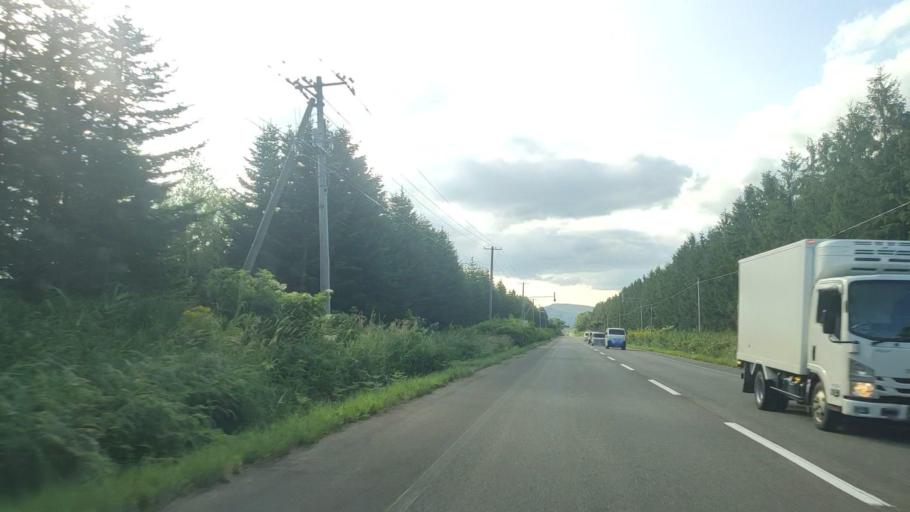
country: JP
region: Hokkaido
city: Makubetsu
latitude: 44.8880
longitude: 142.0059
